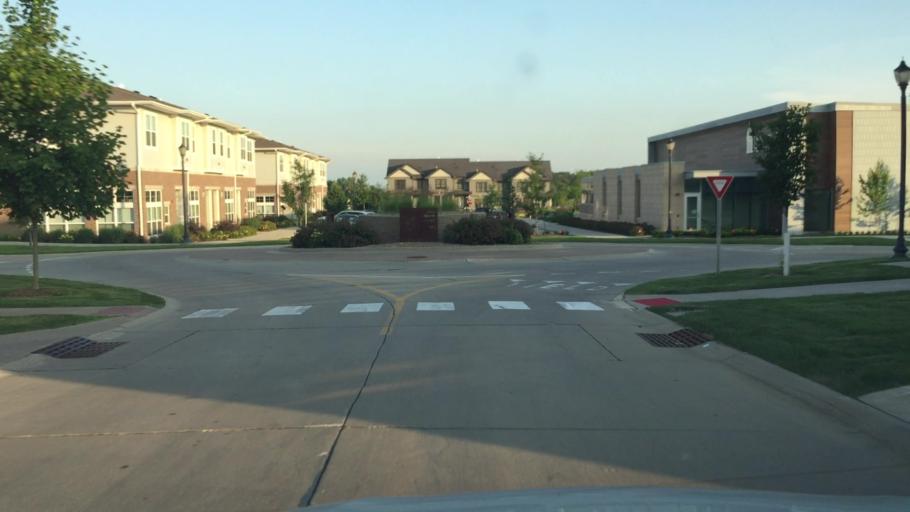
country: US
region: Iowa
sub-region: Johnson County
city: Iowa City
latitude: 41.6687
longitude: -91.4811
